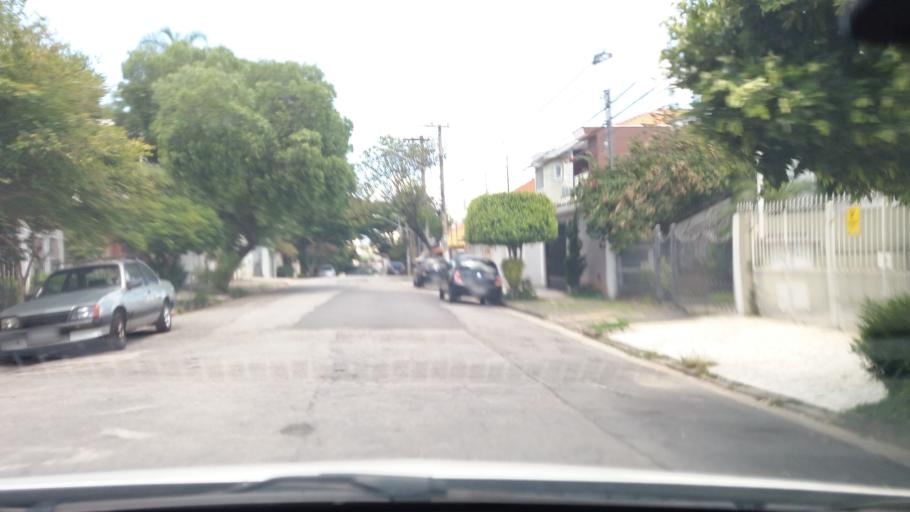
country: BR
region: Sao Paulo
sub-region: Sao Paulo
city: Sao Paulo
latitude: -23.4805
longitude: -46.6194
